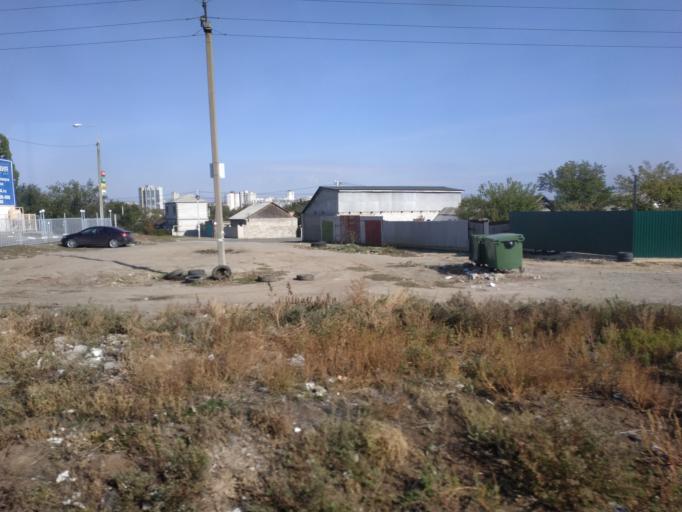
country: RU
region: Volgograd
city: Volgograd
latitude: 48.7500
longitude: 44.5328
